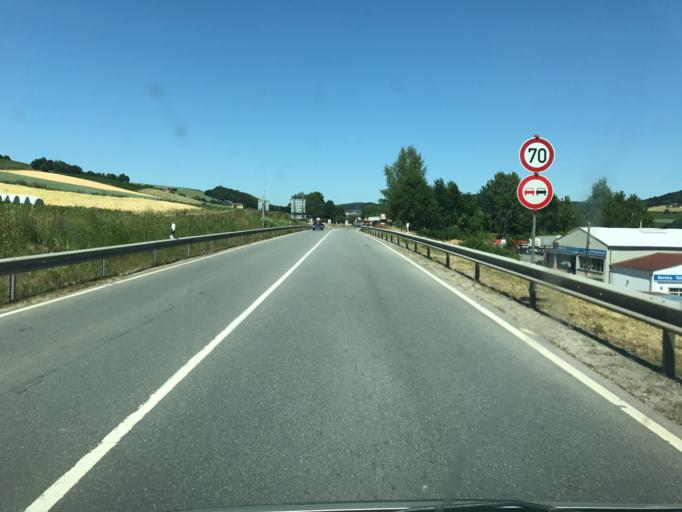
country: DE
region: Bavaria
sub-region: Upper Palatinate
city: Furth im Wald
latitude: 49.3180
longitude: 12.8466
